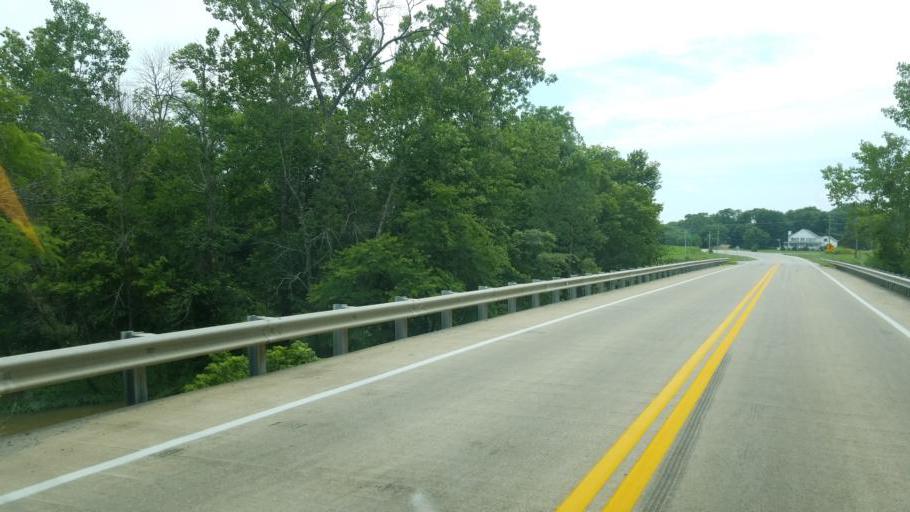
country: US
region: Ohio
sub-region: Madison County
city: Plain City
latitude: 40.0408
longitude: -83.2530
